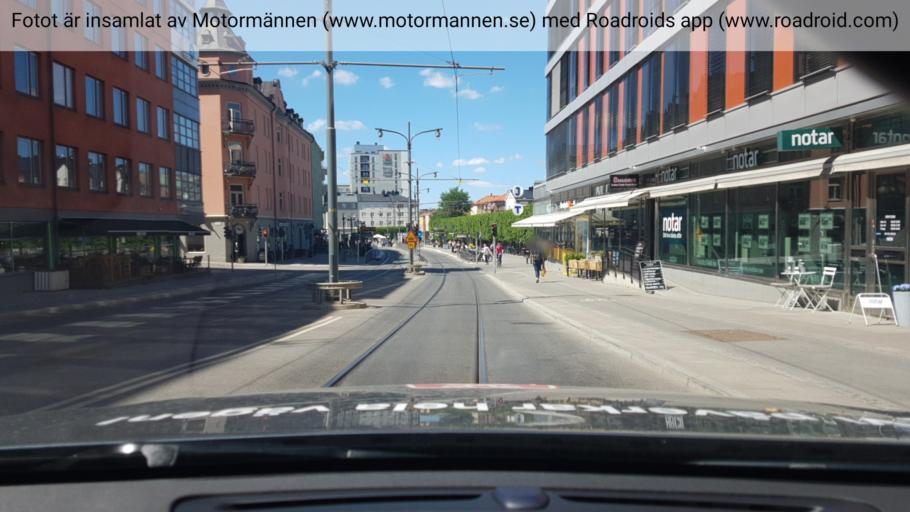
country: SE
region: Stockholm
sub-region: Sundbybergs Kommun
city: Sundbyberg
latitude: 59.3603
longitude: 17.9718
